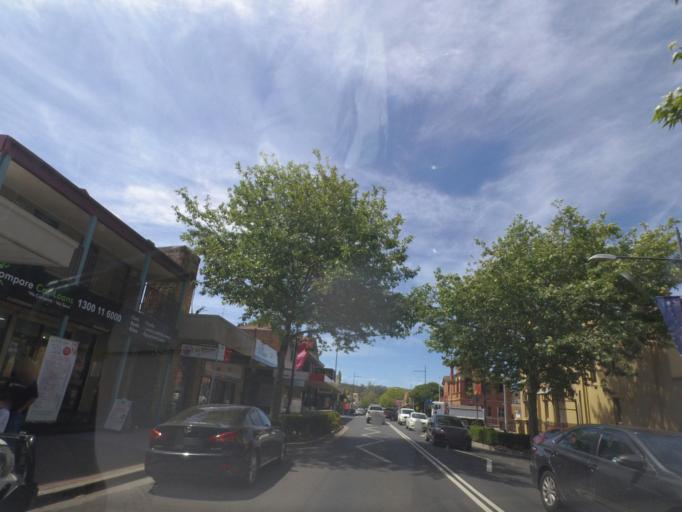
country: AU
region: New South Wales
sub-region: Wollondilly
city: Picton
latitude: -34.1699
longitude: 150.6111
